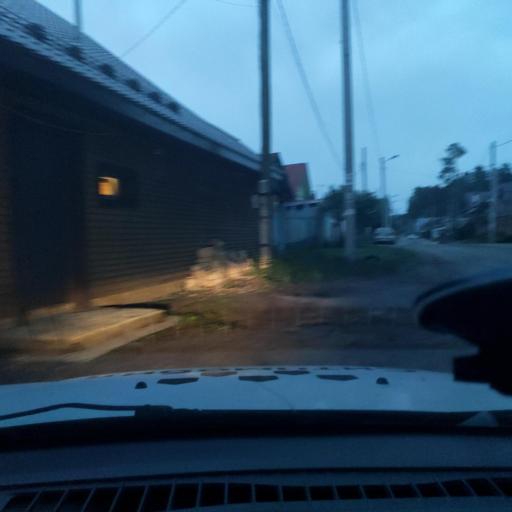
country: RU
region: Perm
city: Kondratovo
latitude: 58.0322
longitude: 56.0040
